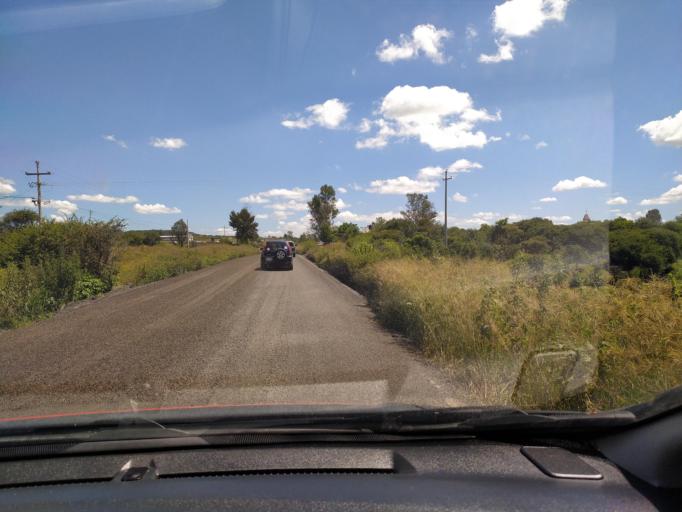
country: MX
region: Jalisco
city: San Julian
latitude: 21.0012
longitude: -102.0937
